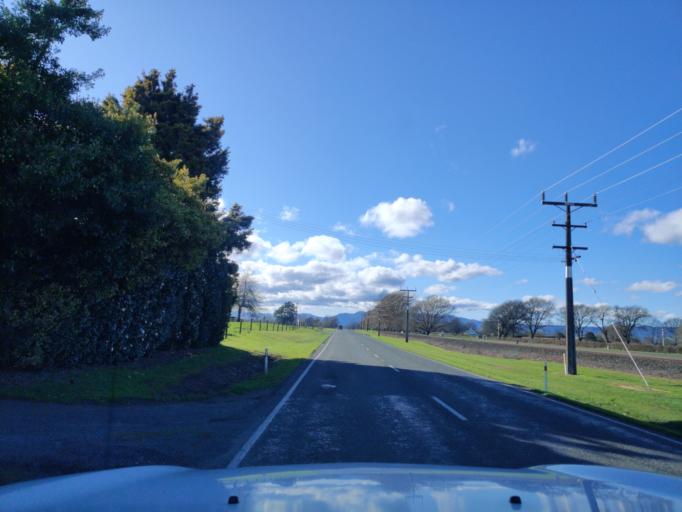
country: NZ
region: Waikato
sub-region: Matamata-Piako District
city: Matamata
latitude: -37.8459
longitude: 175.7612
